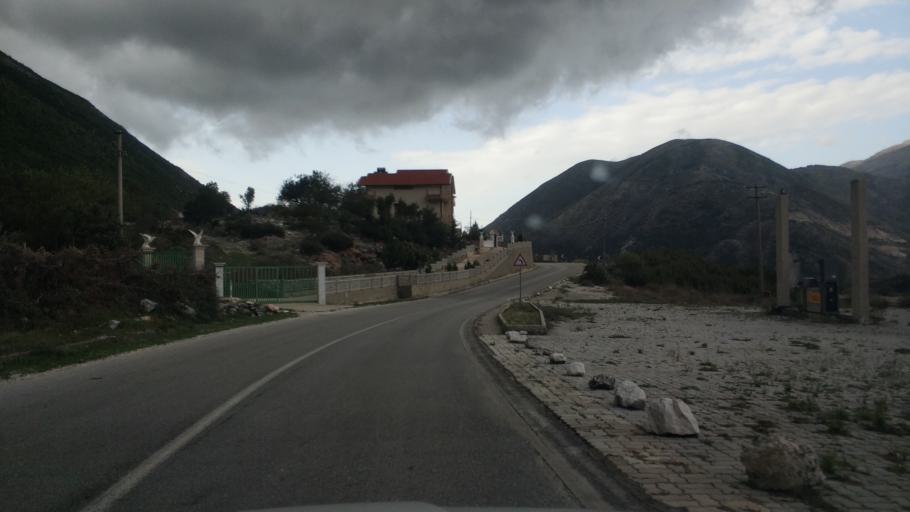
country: AL
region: Vlore
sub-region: Rrethi i Vlores
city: Brataj
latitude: 40.2354
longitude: 19.5554
